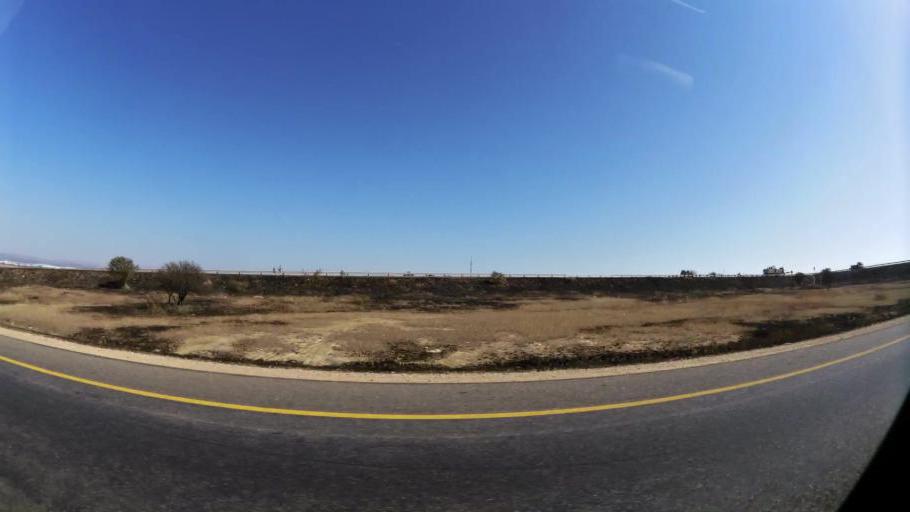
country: ZA
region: Gauteng
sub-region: City of Tshwane Metropolitan Municipality
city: Mabopane
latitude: -25.5812
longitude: 28.1097
